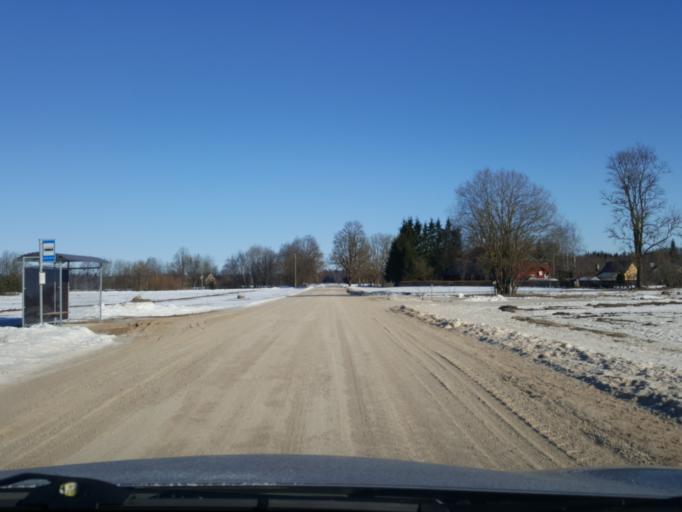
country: EE
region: Viljandimaa
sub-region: Viljandi linn
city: Viljandi
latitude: 58.4518
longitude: 25.5335
